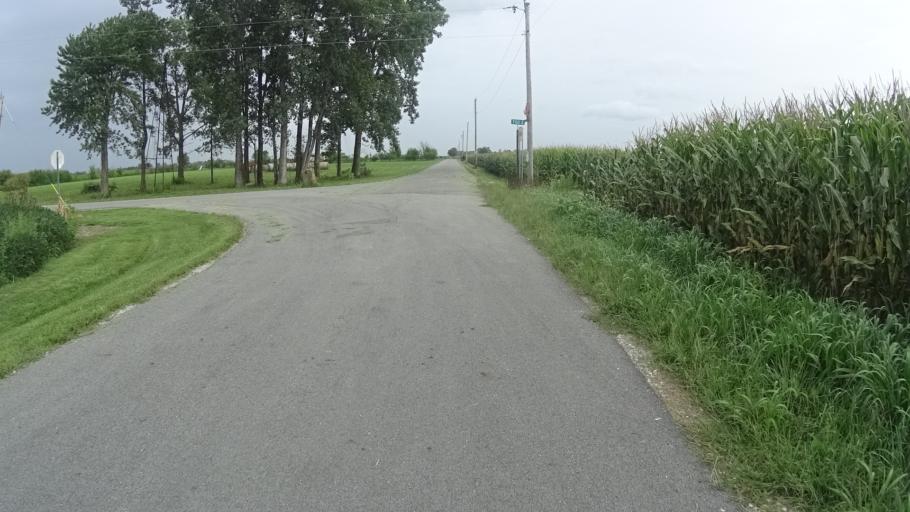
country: US
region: Indiana
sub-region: Madison County
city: Ingalls
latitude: 40.0022
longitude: -85.8148
